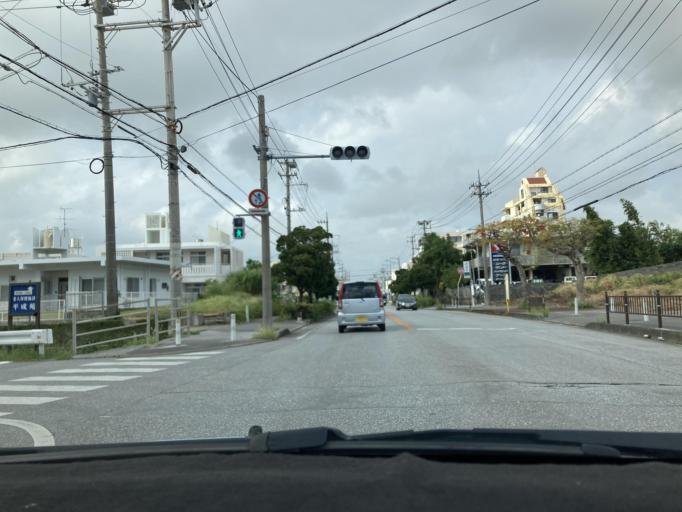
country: JP
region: Okinawa
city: Itoman
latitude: 26.1538
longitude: 127.6715
